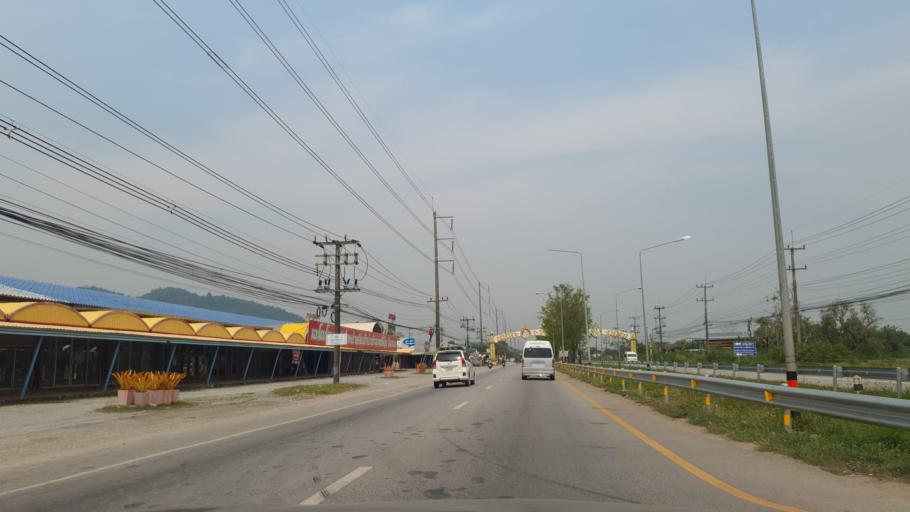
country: TH
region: Rayong
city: Rayong
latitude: 12.6408
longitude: 101.3997
